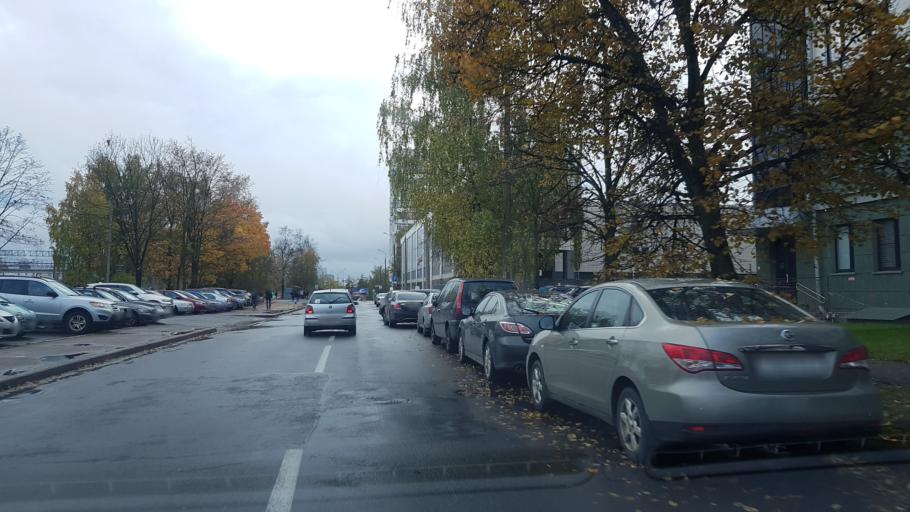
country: BY
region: Minsk
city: Minsk
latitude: 53.8929
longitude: 27.5888
